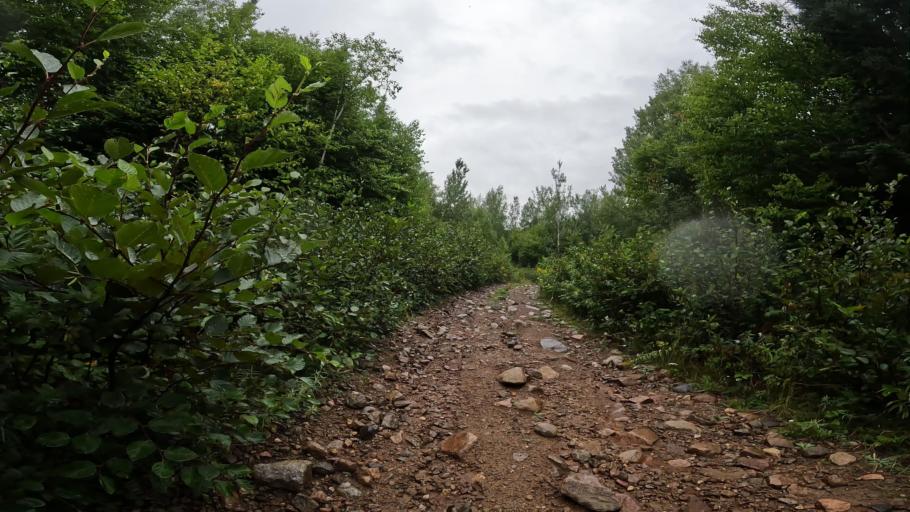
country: CA
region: Quebec
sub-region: Capitale-Nationale
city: La Malbaie
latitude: 47.8124
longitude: -70.4847
